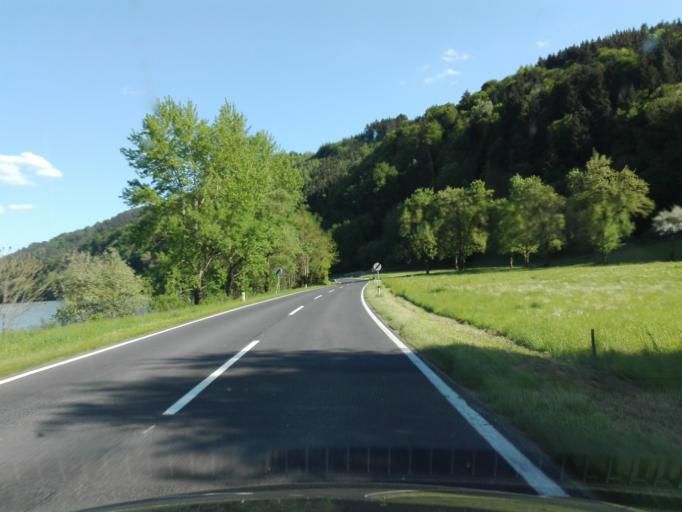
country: AT
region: Upper Austria
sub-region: Politischer Bezirk Rohrbach
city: Pfarrkirchen im Muehlkreis
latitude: 48.4706
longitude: 13.7742
